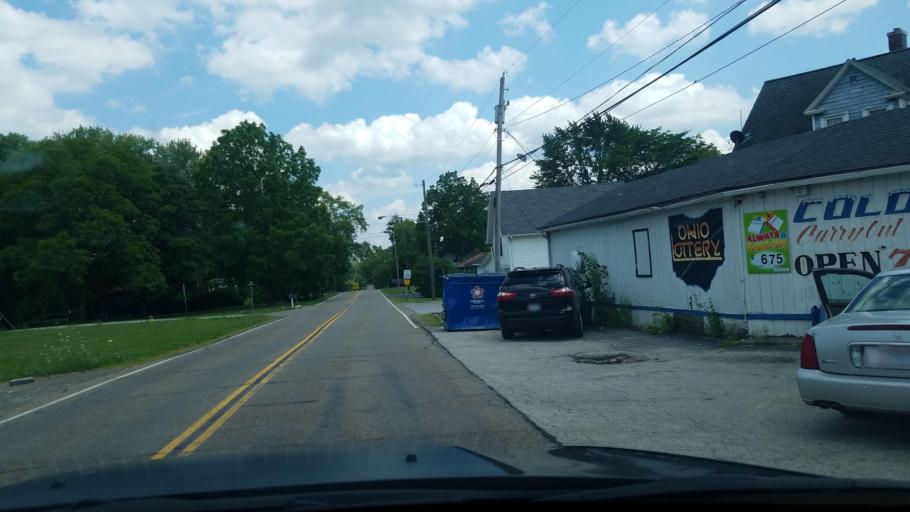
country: US
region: Ohio
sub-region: Trumbull County
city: Bolindale
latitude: 41.2032
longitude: -80.7793
